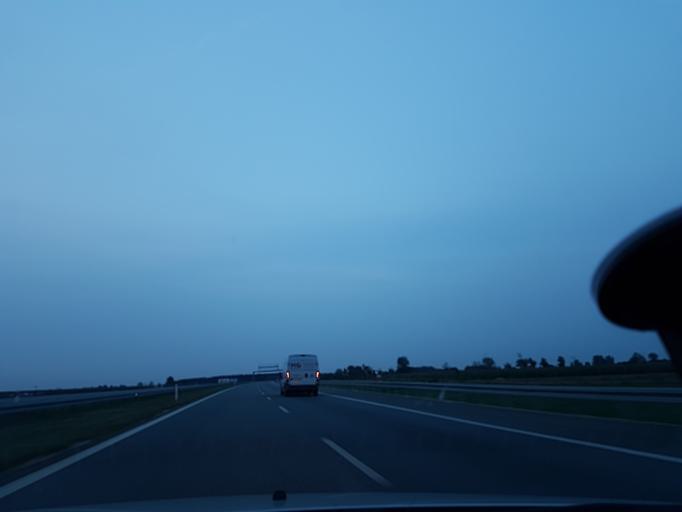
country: PL
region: Lodz Voivodeship
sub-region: Powiat leczycki
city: Piatek
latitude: 52.0792
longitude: 19.5304
